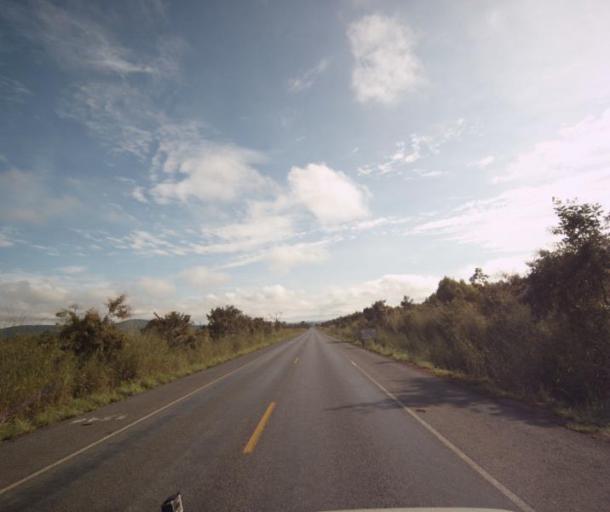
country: BR
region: Goias
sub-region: Pirenopolis
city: Pirenopolis
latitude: -15.5164
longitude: -48.6232
